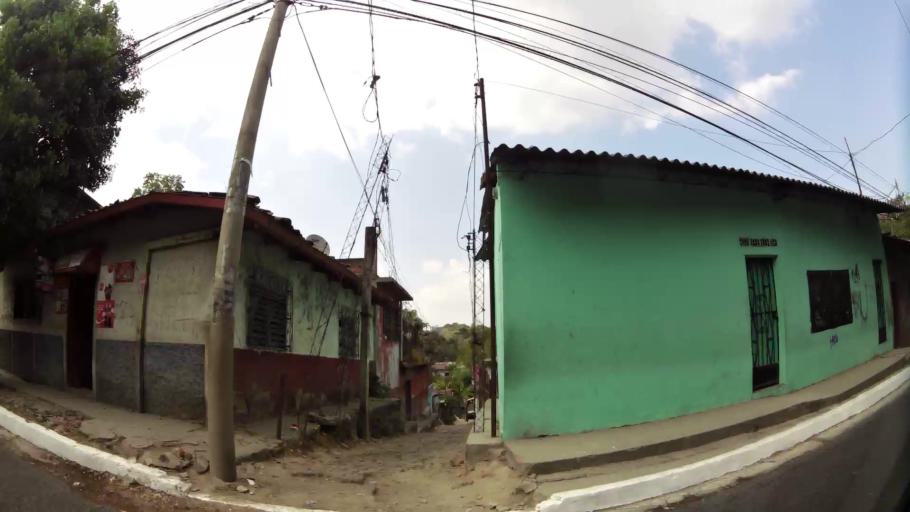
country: SV
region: San Salvador
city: Delgado
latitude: 13.7185
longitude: -89.1635
